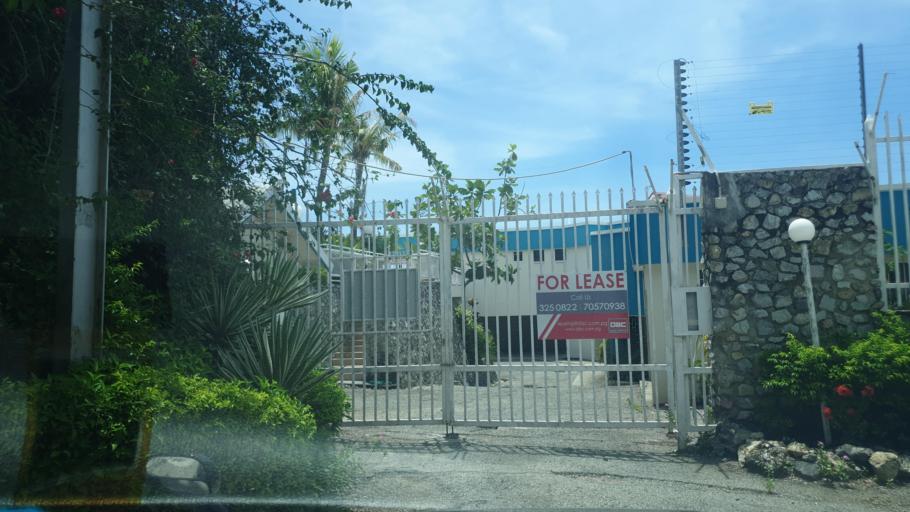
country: PG
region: National Capital
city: Port Moresby
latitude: -9.4755
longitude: 147.1587
